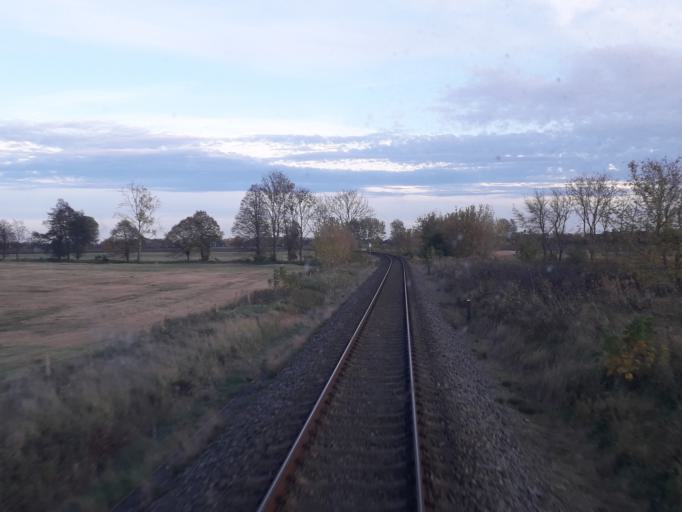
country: DE
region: Brandenburg
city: Dabergotz
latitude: 52.9357
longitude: 12.7143
